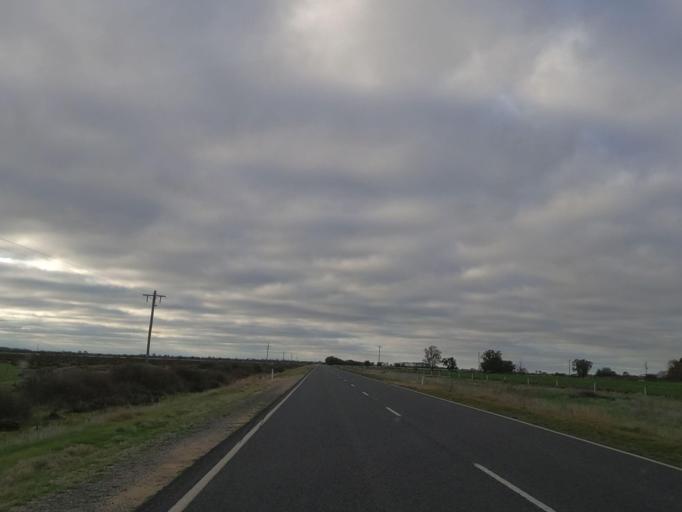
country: AU
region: Victoria
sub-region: Swan Hill
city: Swan Hill
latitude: -35.8375
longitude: 143.9412
